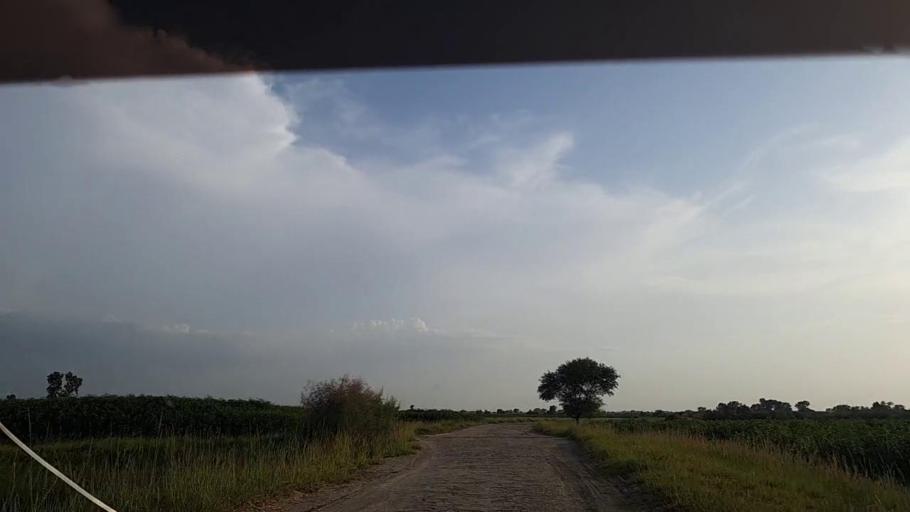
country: PK
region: Sindh
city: Khanpur
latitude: 27.8046
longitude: 69.3162
